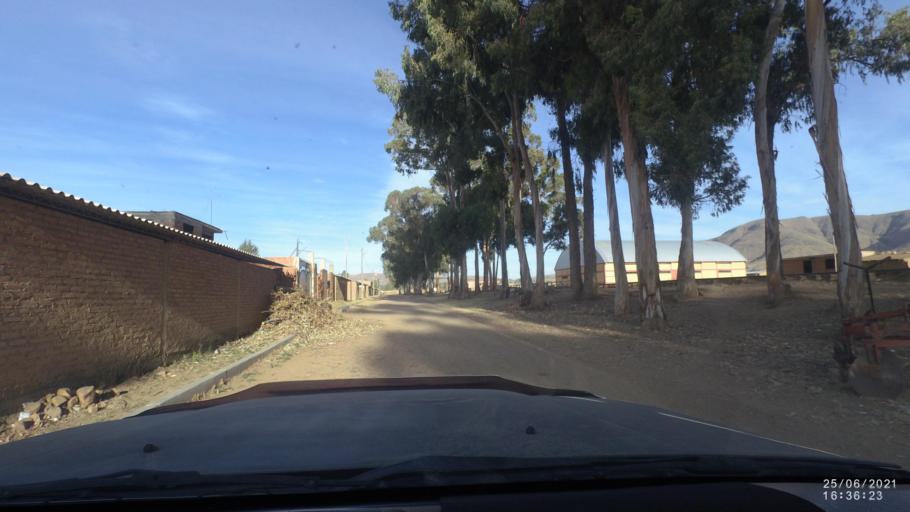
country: BO
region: Cochabamba
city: Arani
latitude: -17.8186
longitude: -65.7771
